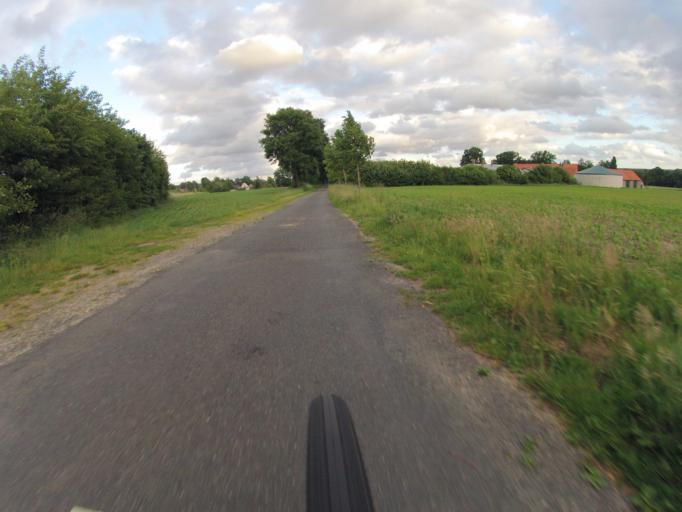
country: DE
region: North Rhine-Westphalia
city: Ibbenburen
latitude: 52.2925
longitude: 7.6846
